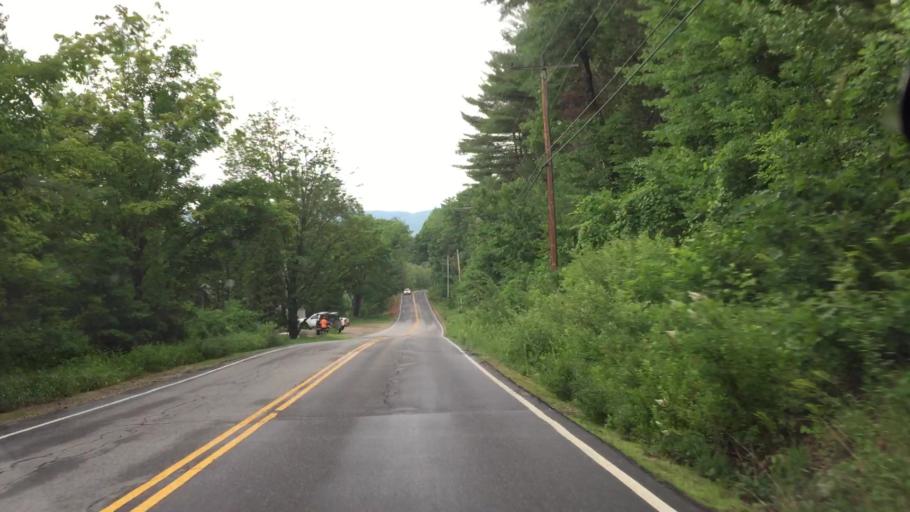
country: US
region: New Hampshire
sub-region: Carroll County
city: Center Harbor
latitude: 43.7490
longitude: -71.4796
